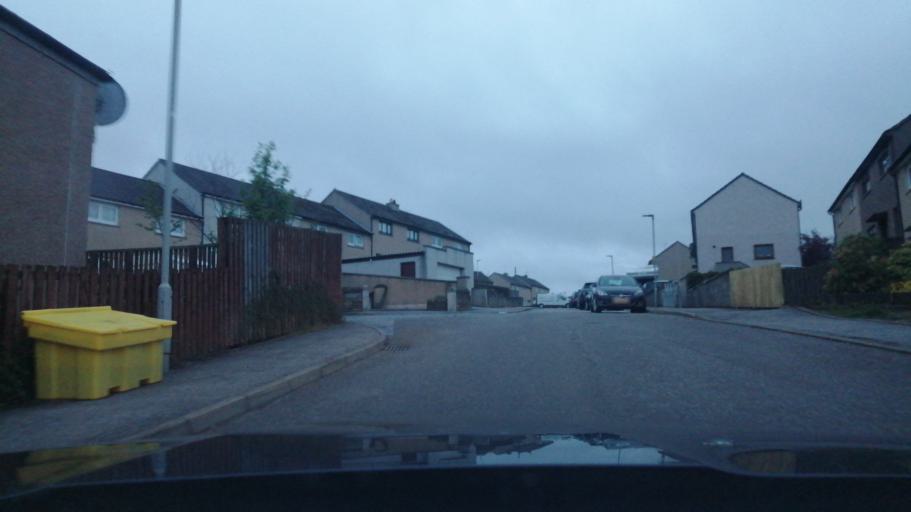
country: GB
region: Scotland
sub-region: Moray
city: Keith
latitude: 57.5415
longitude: -2.9560
